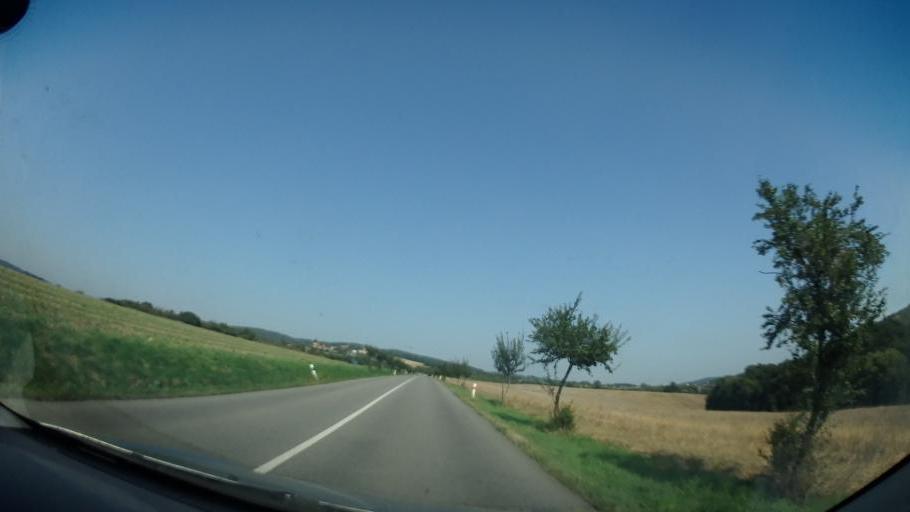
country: CZ
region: South Moravian
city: Kurim
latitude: 49.2474
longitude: 16.5285
